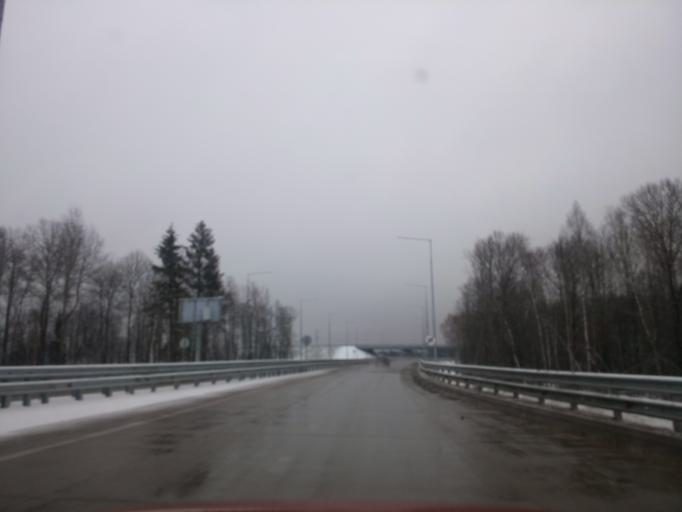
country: RU
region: Tverskaya
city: Likhoslavl'
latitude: 56.9535
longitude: 35.5107
